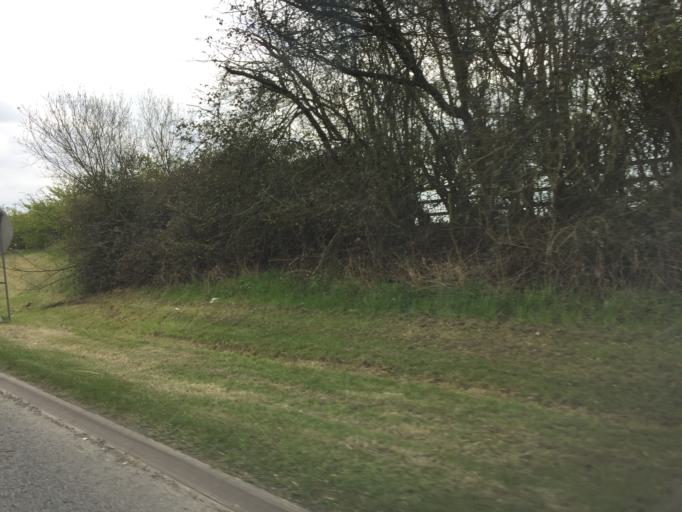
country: GB
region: England
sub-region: Buckinghamshire
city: Buckingham
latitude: 51.9948
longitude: -1.0025
